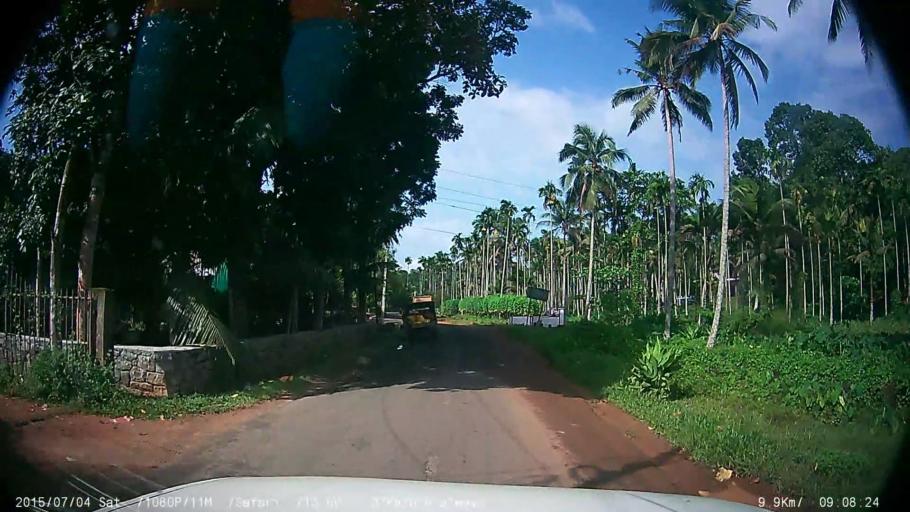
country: IN
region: Kerala
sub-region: Kottayam
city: Palackattumala
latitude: 9.7405
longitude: 76.6118
